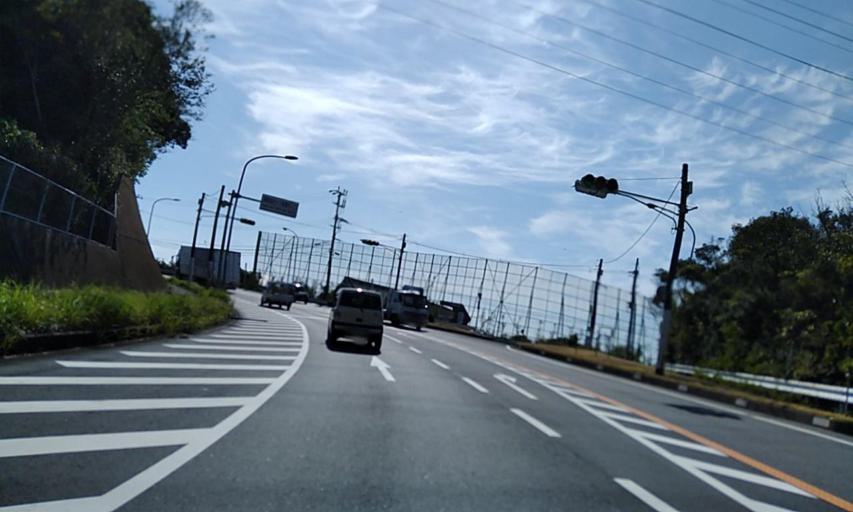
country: JP
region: Wakayama
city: Gobo
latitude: 33.8593
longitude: 135.1609
